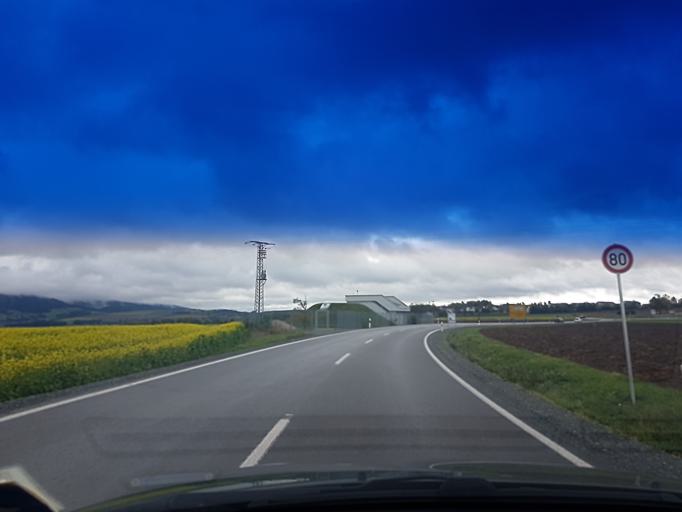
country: DE
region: Bavaria
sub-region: Upper Franconia
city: Bindlach
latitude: 50.0048
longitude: 11.6227
